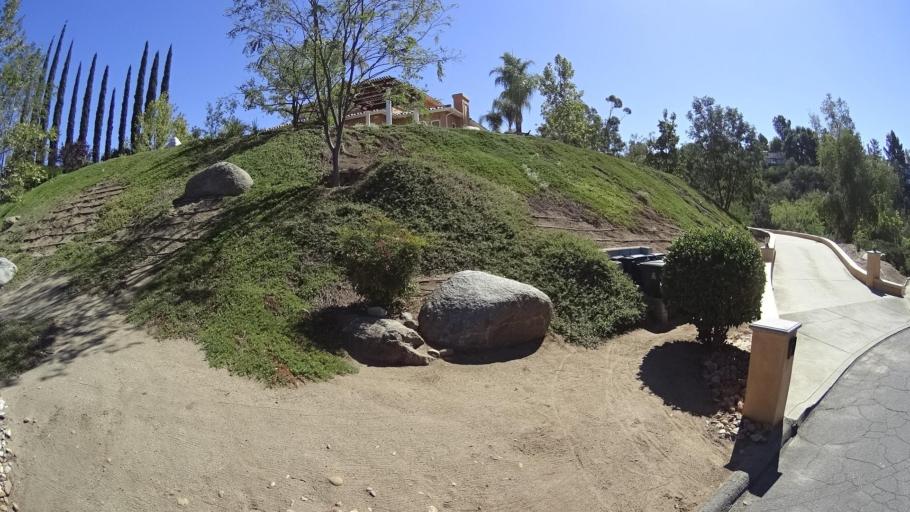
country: US
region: California
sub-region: San Diego County
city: Alpine
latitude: 32.8489
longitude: -116.7649
